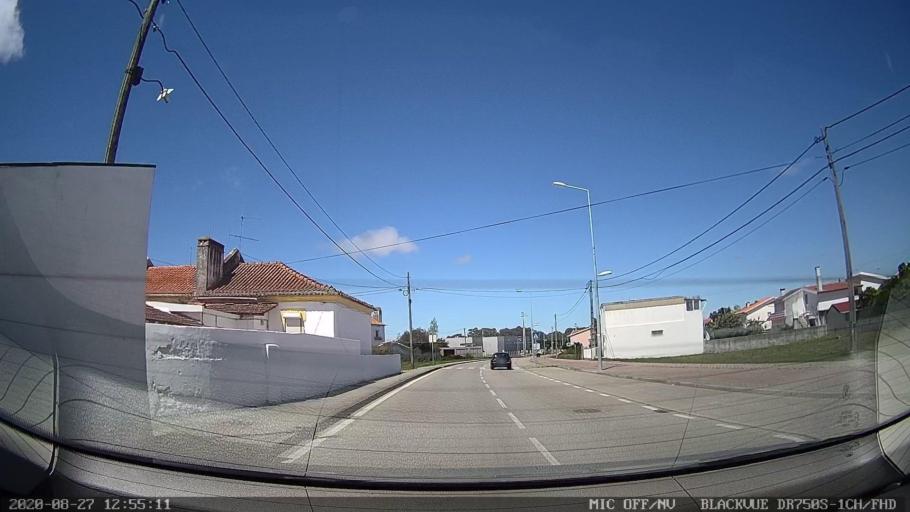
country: PT
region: Aveiro
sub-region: Ilhavo
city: Ilhavo
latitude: 40.5891
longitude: -8.6798
